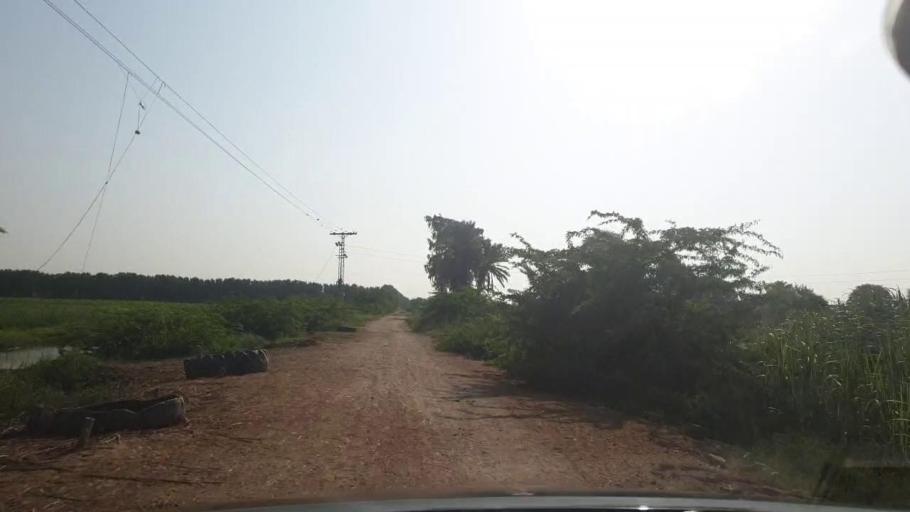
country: PK
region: Sindh
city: Tando Bago
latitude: 24.6509
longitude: 69.1769
